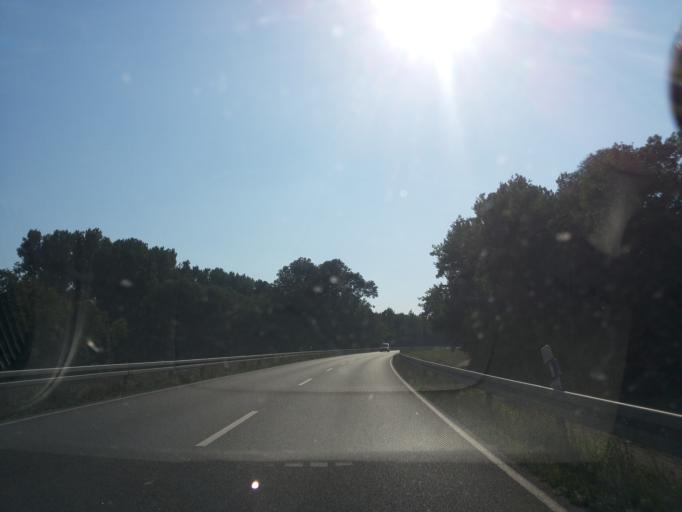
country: DE
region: Bavaria
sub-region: Upper Bavaria
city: Munchsmunster
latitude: 48.7912
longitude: 11.6827
